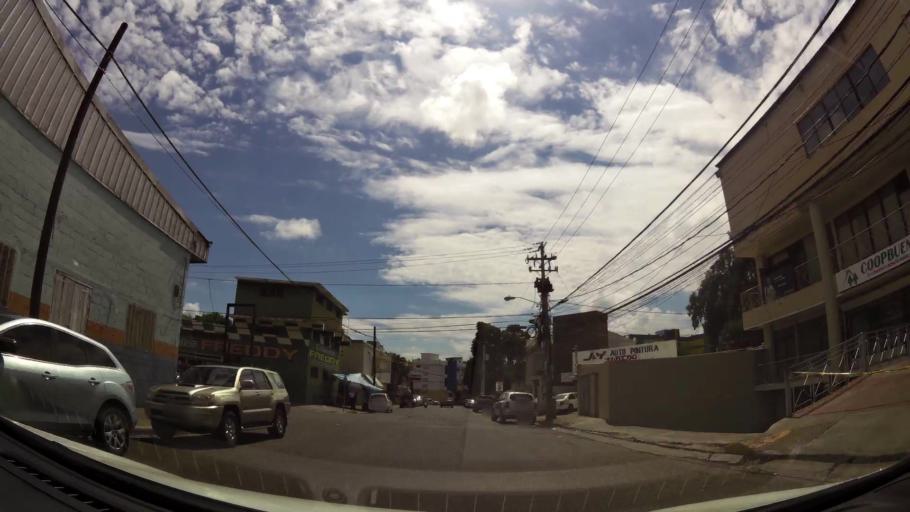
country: DO
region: Santiago
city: Santiago de los Caballeros
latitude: 19.4580
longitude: -70.7003
